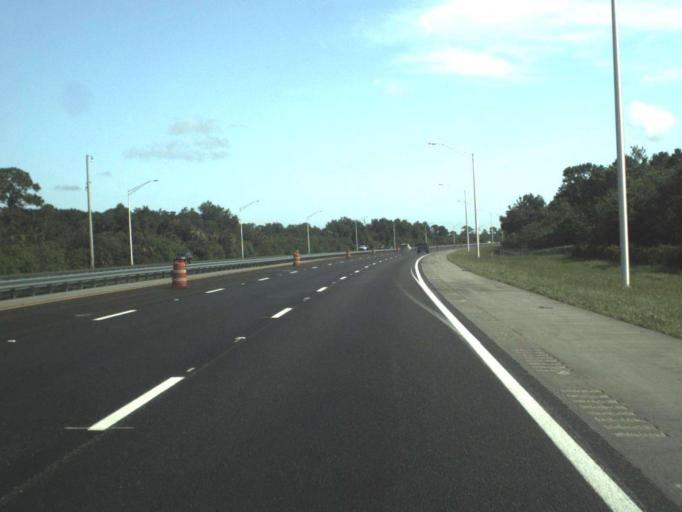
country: US
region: Florida
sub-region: Indian River County
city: West Vero Corridor
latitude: 27.6158
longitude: -80.5144
